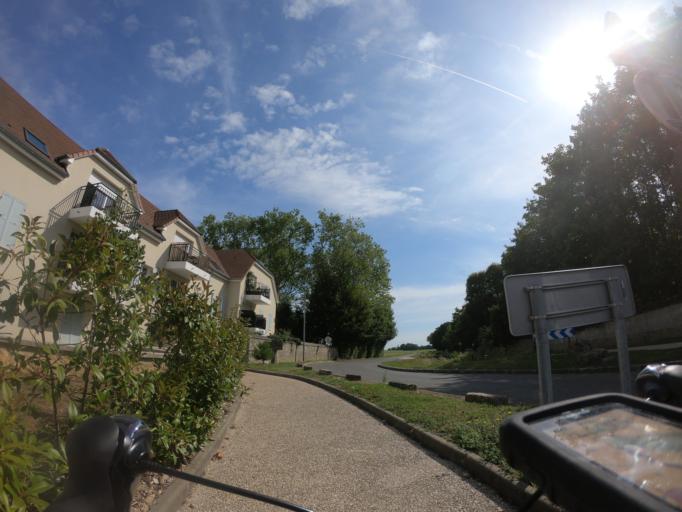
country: FR
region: Ile-de-France
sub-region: Departement de l'Essonne
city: Villiers-le-Bacle
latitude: 48.7258
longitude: 2.1270
